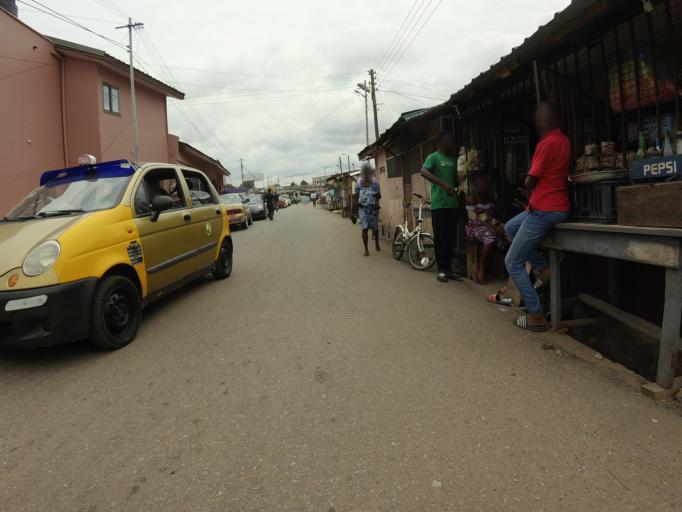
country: GH
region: Greater Accra
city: Accra
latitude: 5.5908
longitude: -0.2157
